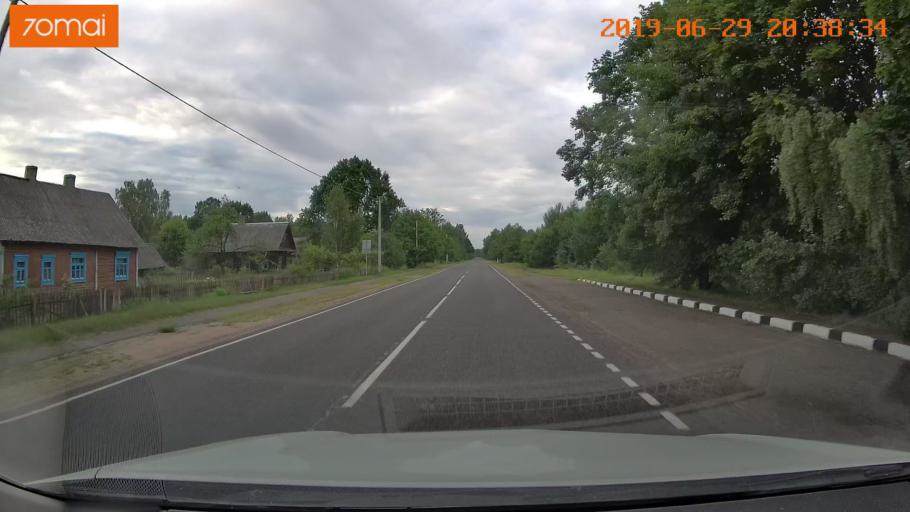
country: BY
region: Brest
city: Hantsavichy
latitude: 52.5516
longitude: 26.3644
